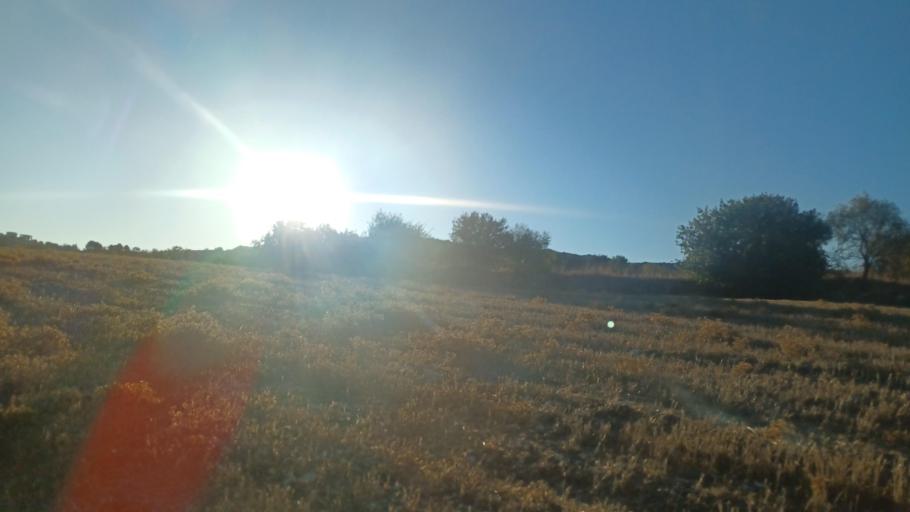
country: CY
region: Pafos
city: Mesogi
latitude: 34.7923
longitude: 32.4734
